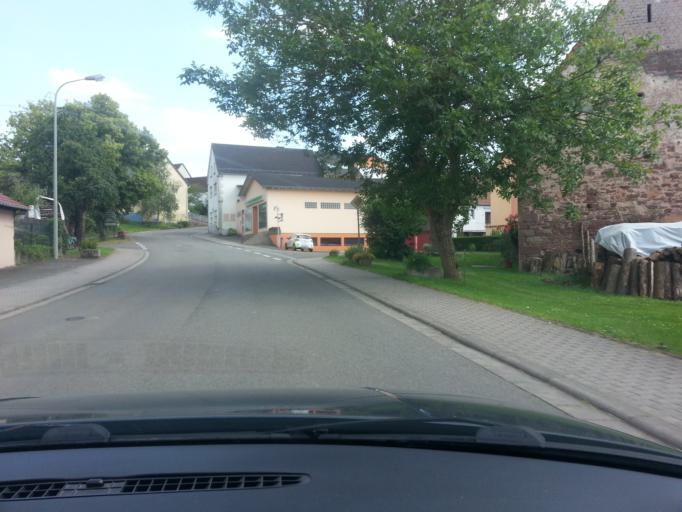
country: DE
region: Rheinland-Pfalz
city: Bottenbach
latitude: 49.1837
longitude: 7.4943
